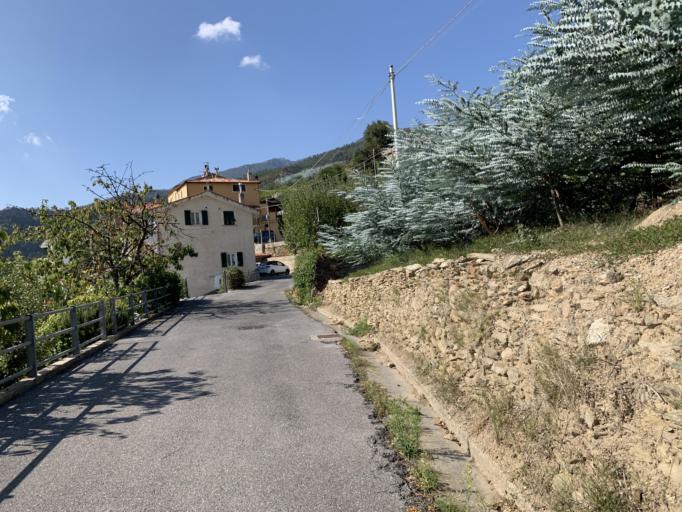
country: IT
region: Liguria
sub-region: Provincia di Savona
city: Magliolo
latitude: 44.1908
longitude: 8.2441
